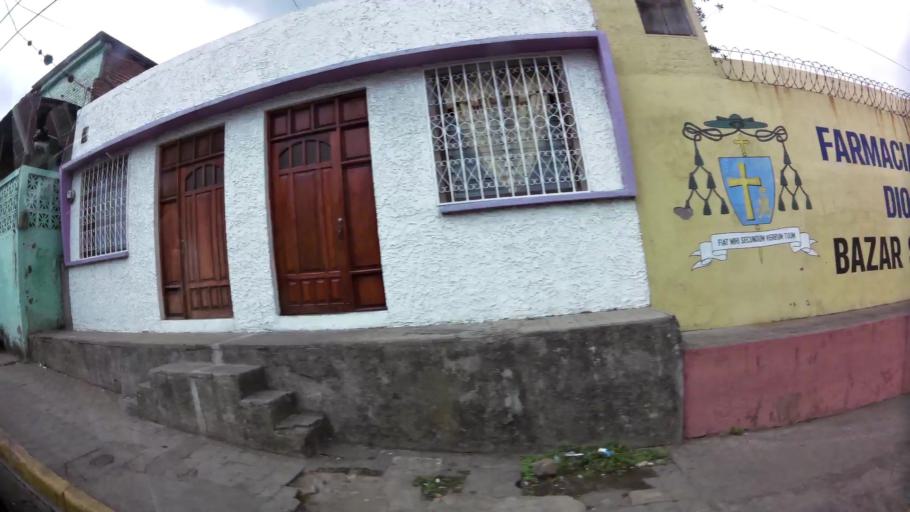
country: NI
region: Matagalpa
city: Matagalpa
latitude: 12.9188
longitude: -85.9243
